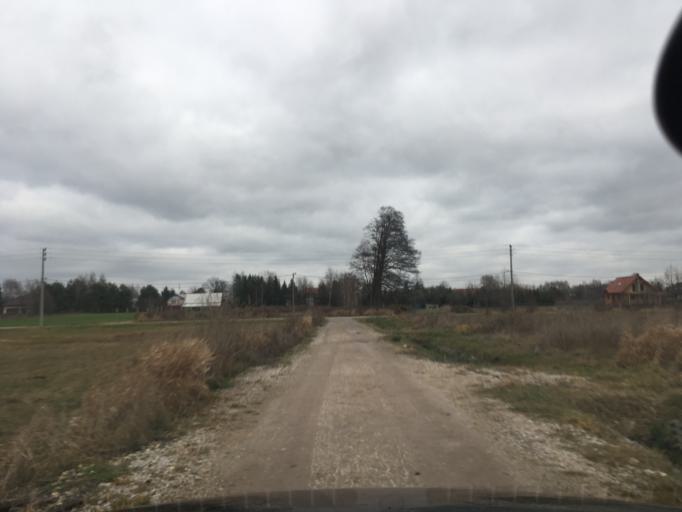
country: PL
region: Masovian Voivodeship
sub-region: Powiat piaseczynski
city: Lesznowola
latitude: 52.0487
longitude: 20.9268
